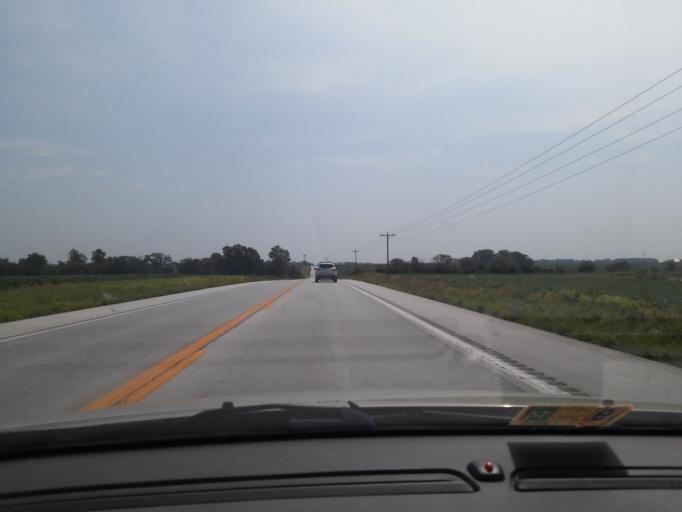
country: US
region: Missouri
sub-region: Montgomery County
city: Wellsville
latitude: 39.1632
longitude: -91.6659
